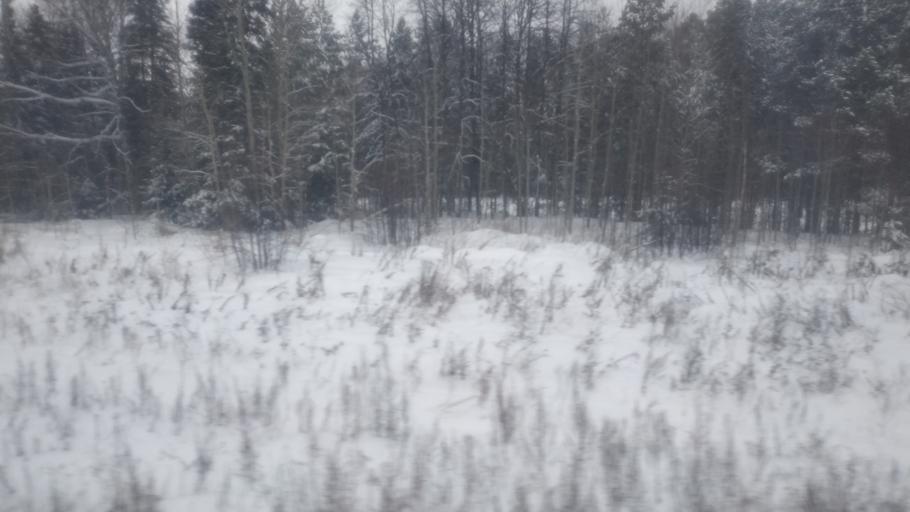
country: RU
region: Udmurtiya
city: Malaya Purga
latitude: 56.5527
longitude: 53.0995
